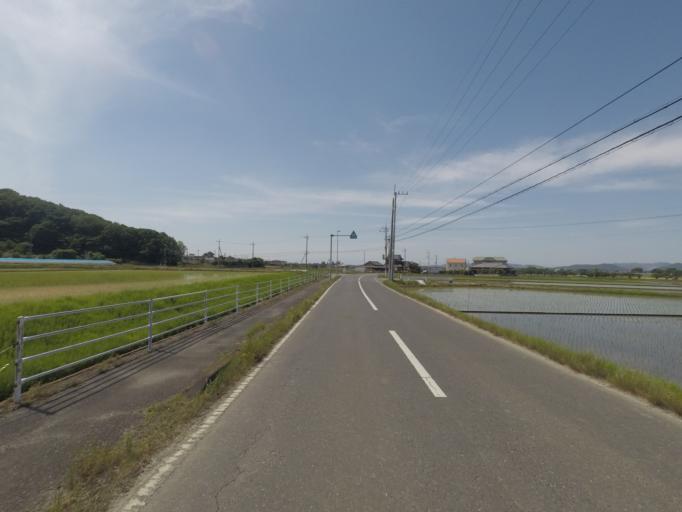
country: JP
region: Ibaraki
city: Makabe
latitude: 36.2648
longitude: 140.1022
